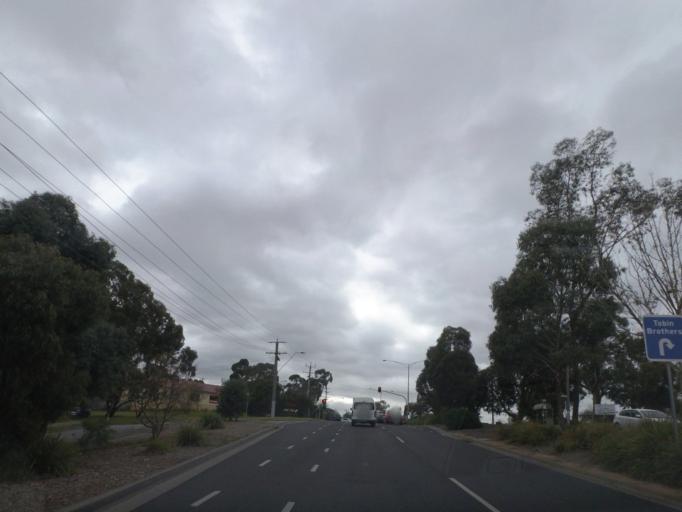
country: AU
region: Victoria
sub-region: Nillumbik
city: Diamond Creek
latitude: -37.6736
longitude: 145.1489
